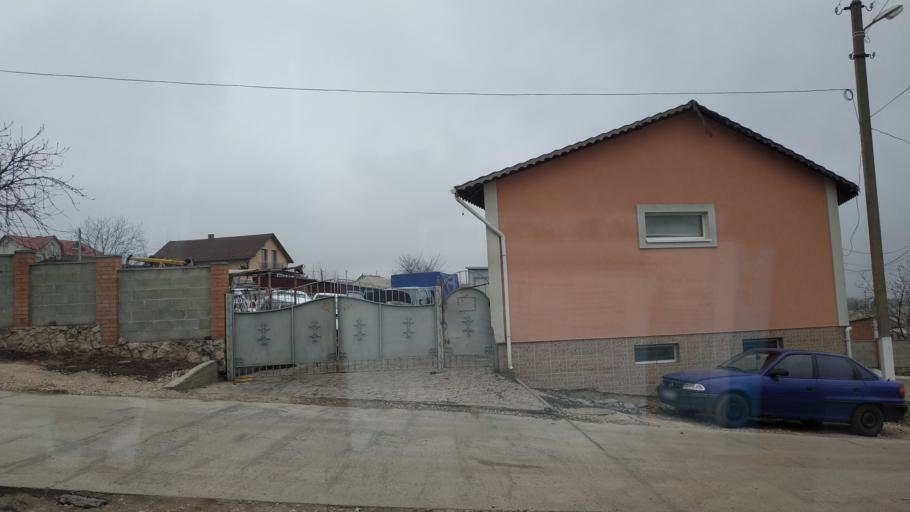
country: MD
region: Hincesti
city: Hincesti
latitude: 46.9090
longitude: 28.6670
